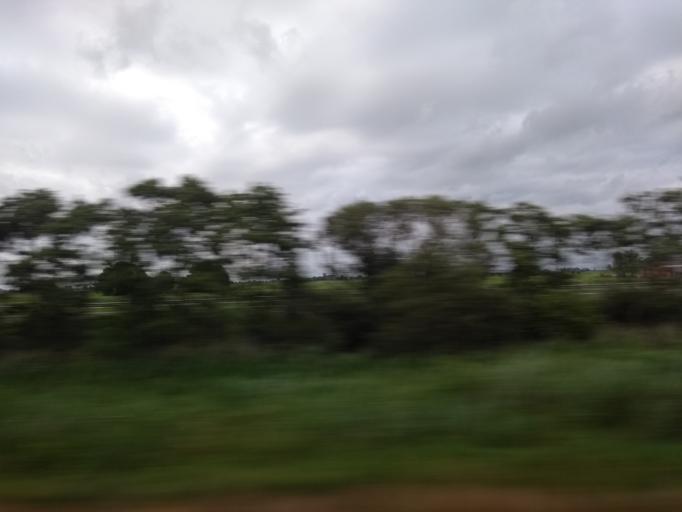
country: NL
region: Friesland
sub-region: Gemeente Boarnsterhim
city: Reduzum
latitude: 53.1260
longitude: 5.8043
